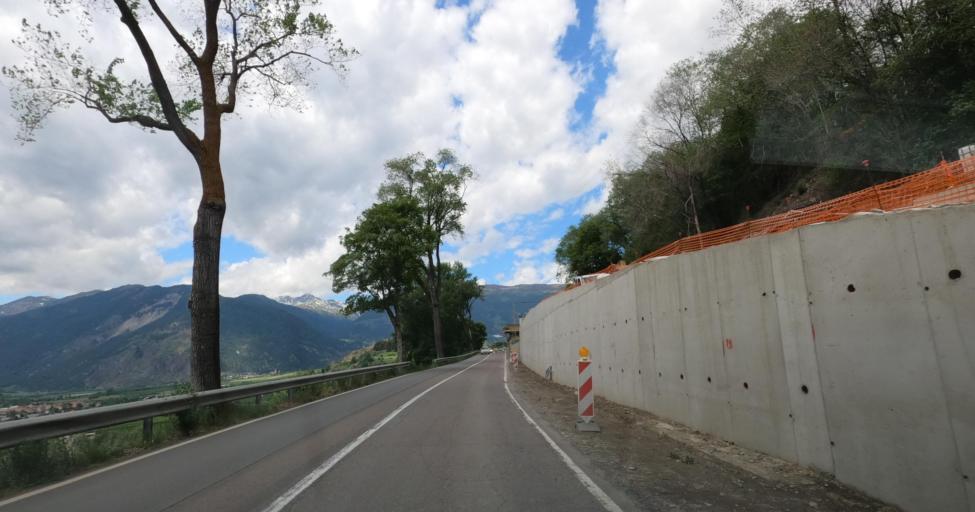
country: IT
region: Trentino-Alto Adige
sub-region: Bolzano
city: Sluderno
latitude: 46.6722
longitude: 10.5780
